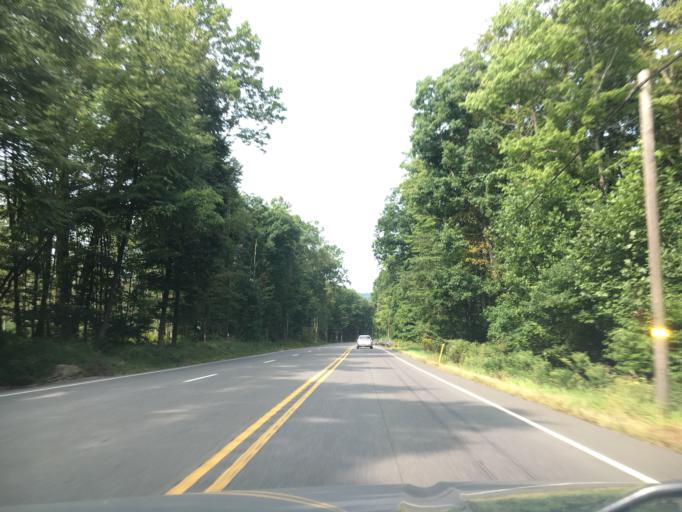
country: US
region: Pennsylvania
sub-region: Carbon County
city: Summit Hill
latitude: 40.7130
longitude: -75.8381
